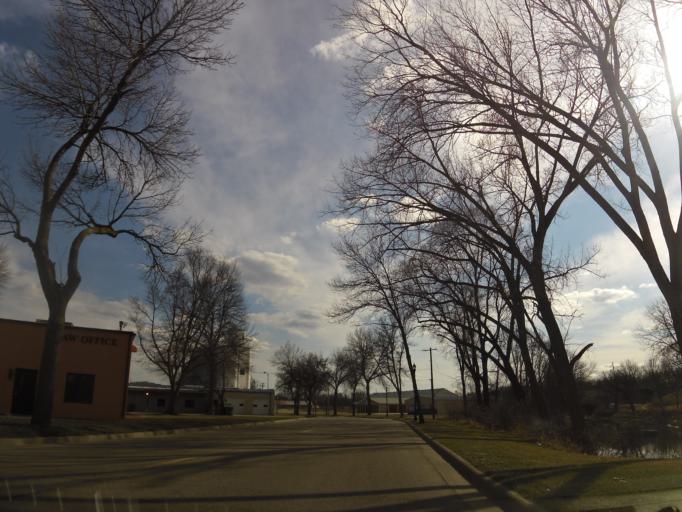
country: US
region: Minnesota
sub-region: Chippewa County
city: Montevideo
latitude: 44.9453
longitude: -95.7258
